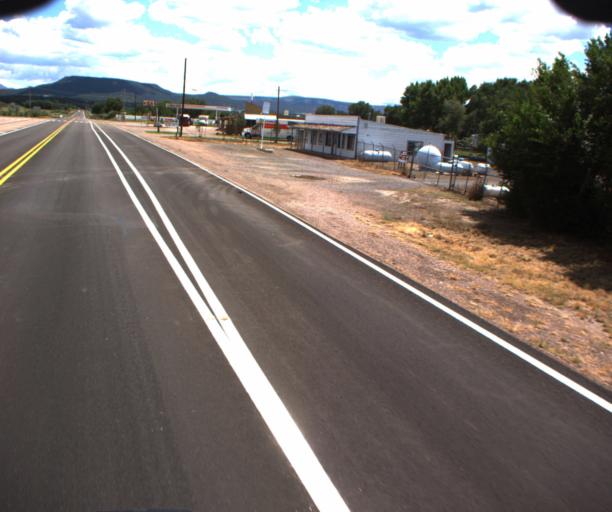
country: US
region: Arizona
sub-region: Apache County
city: Springerville
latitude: 34.1491
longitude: -109.2962
